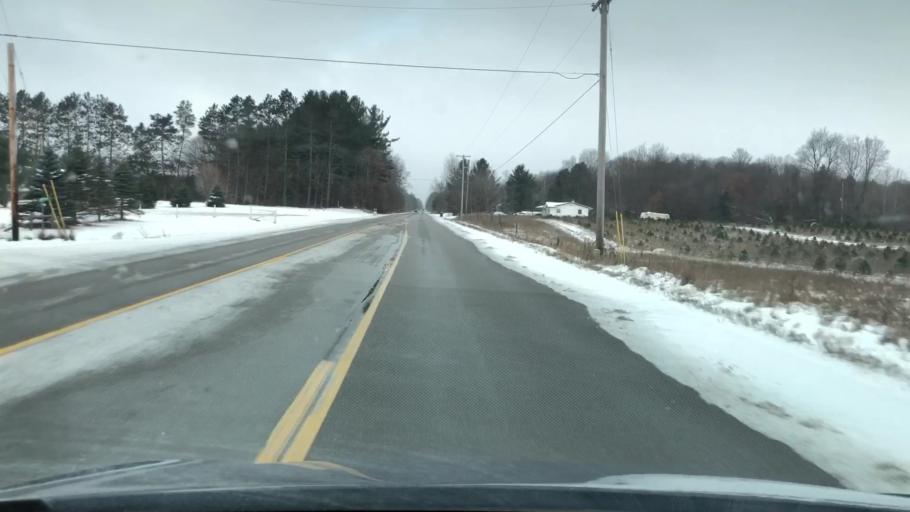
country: US
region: Michigan
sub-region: Wexford County
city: Cadillac
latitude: 44.2812
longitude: -85.4609
